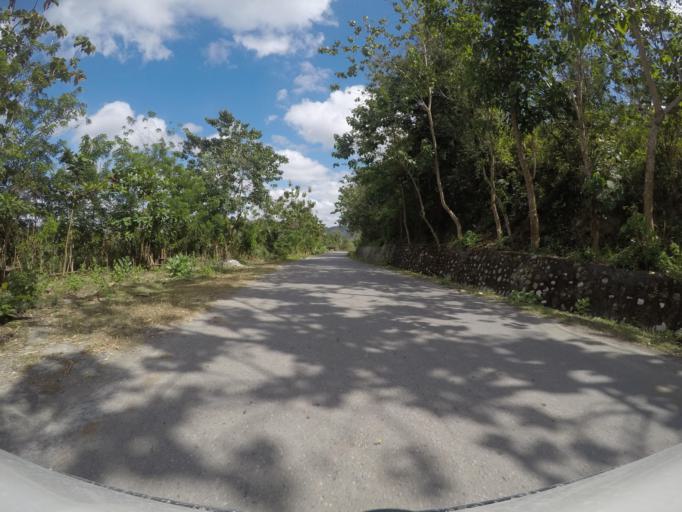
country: TL
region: Viqueque
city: Viqueque
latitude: -8.8724
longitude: 126.3560
